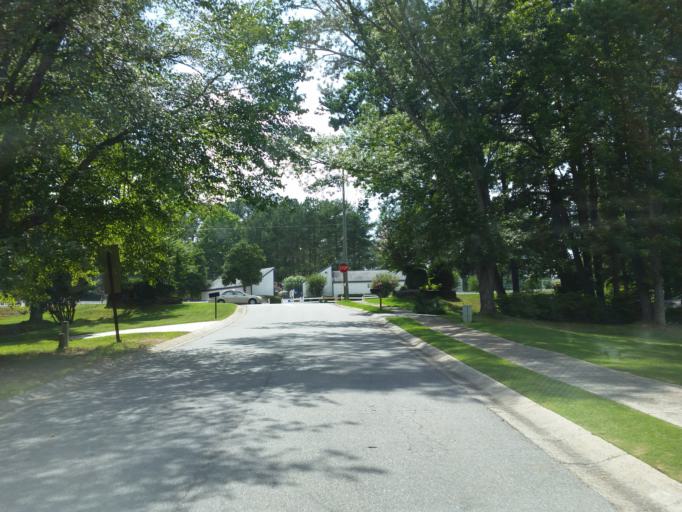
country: US
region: Georgia
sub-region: Cobb County
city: Marietta
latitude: 34.0025
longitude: -84.4722
